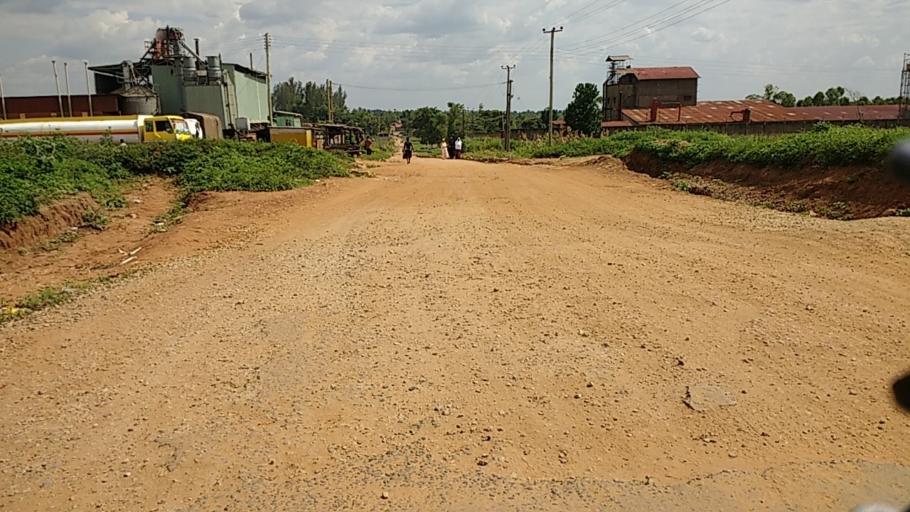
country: UG
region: Eastern Region
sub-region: Mbale District
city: Mbale
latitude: 1.0758
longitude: 34.1596
